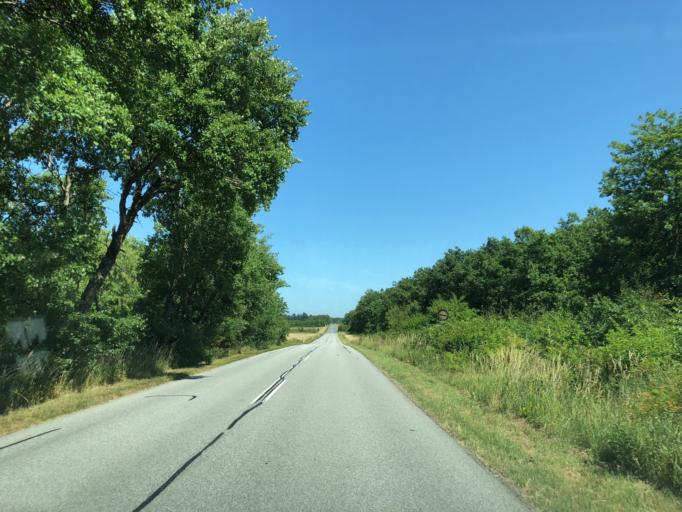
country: DK
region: Central Jutland
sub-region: Skive Kommune
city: Skive
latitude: 56.5206
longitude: 9.0297
